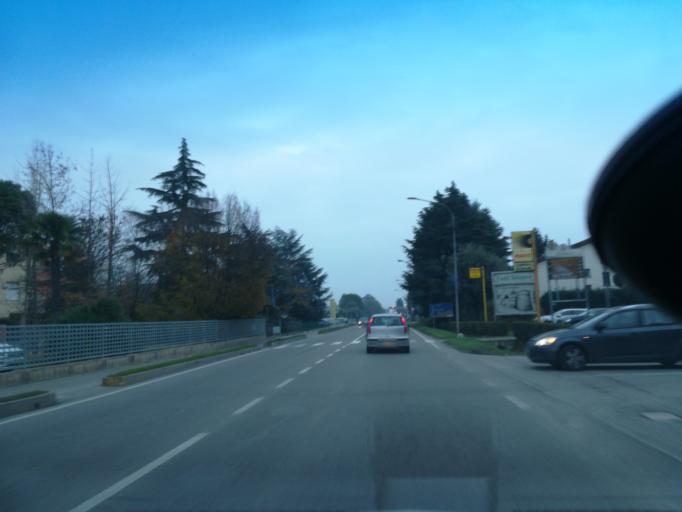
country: IT
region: Emilia-Romagna
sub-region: Provincia di Ravenna
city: Castel Bolognese
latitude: 44.3240
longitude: 11.7886
